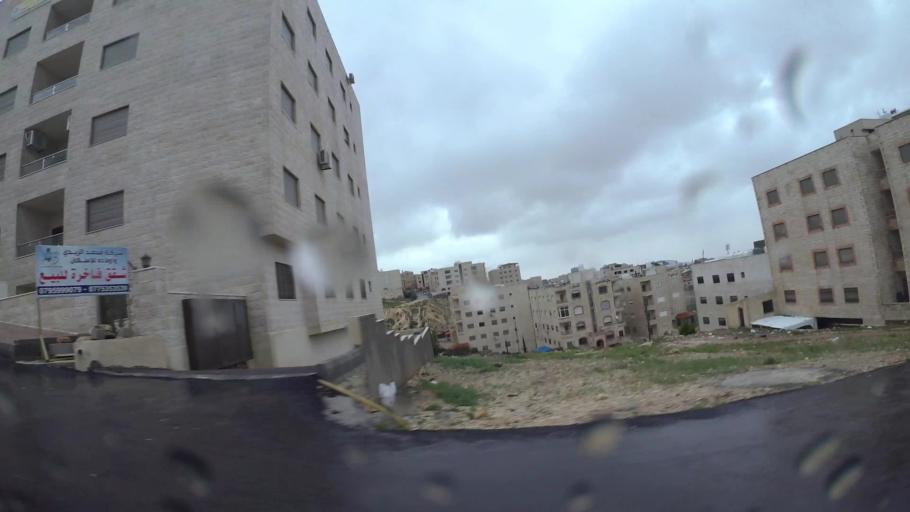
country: JO
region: Amman
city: Al Jubayhah
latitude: 32.0420
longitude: 35.8907
